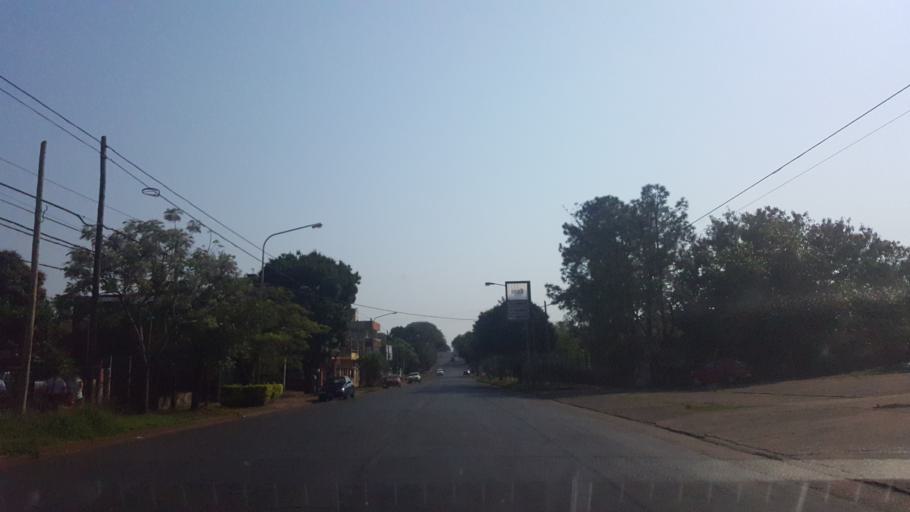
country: AR
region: Misiones
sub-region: Departamento de Capital
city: Posadas
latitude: -27.3833
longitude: -55.9074
